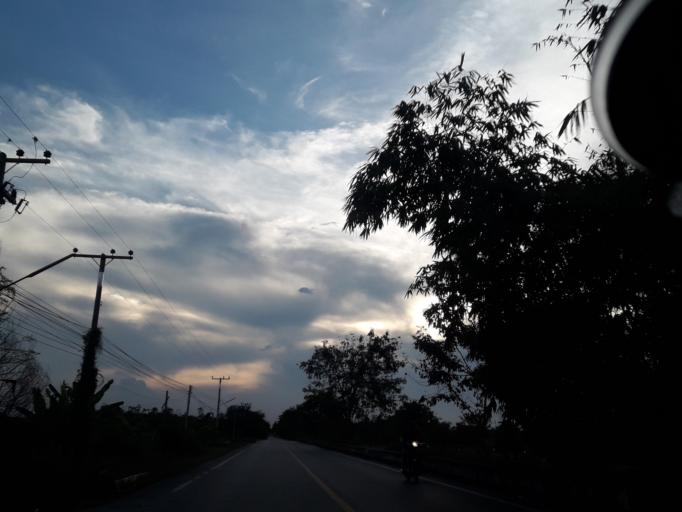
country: TH
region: Sara Buri
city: Nong Khae
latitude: 14.2714
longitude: 100.8823
